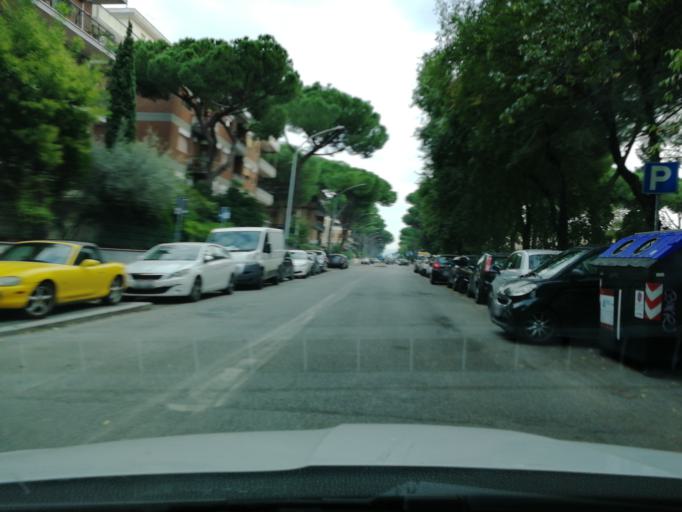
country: IT
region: Latium
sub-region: Citta metropolitana di Roma Capitale
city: Rome
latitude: 41.8521
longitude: 12.5594
